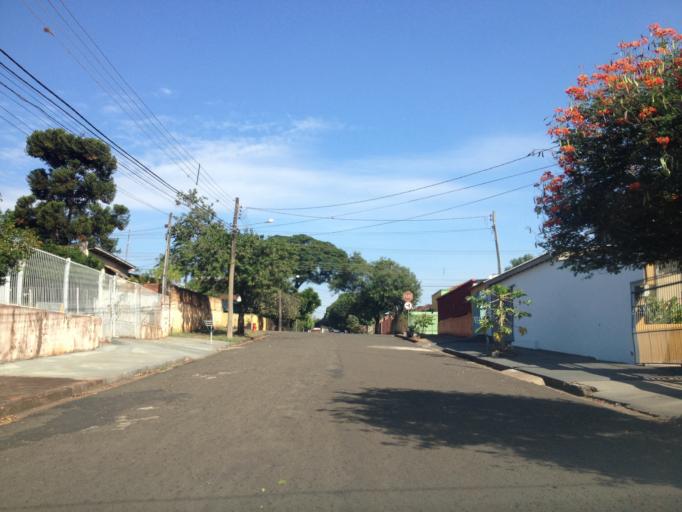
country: BR
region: Parana
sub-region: Londrina
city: Londrina
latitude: -23.2991
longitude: -51.1597
